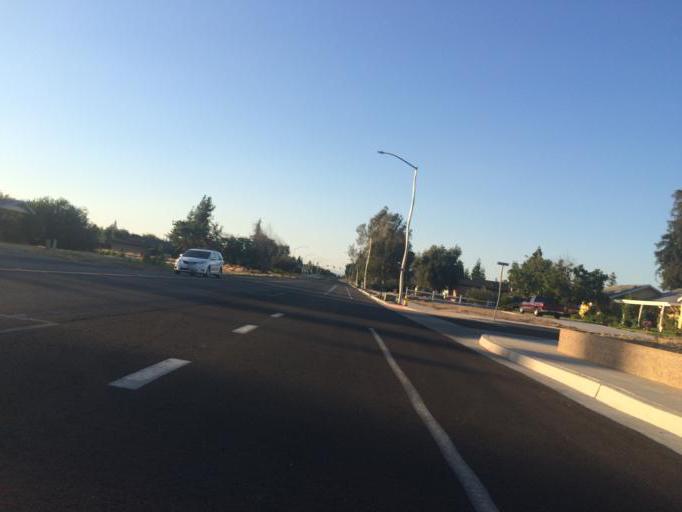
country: US
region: California
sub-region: Fresno County
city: Tarpey Village
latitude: 36.7974
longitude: -119.6730
